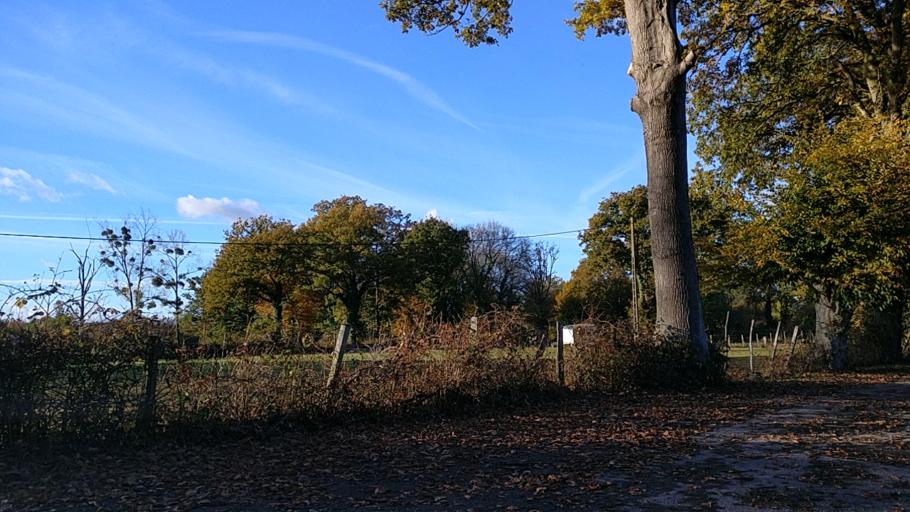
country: FR
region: Brittany
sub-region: Departement d'Ille-et-Vilaine
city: Acigne
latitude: 48.1298
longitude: -1.5671
